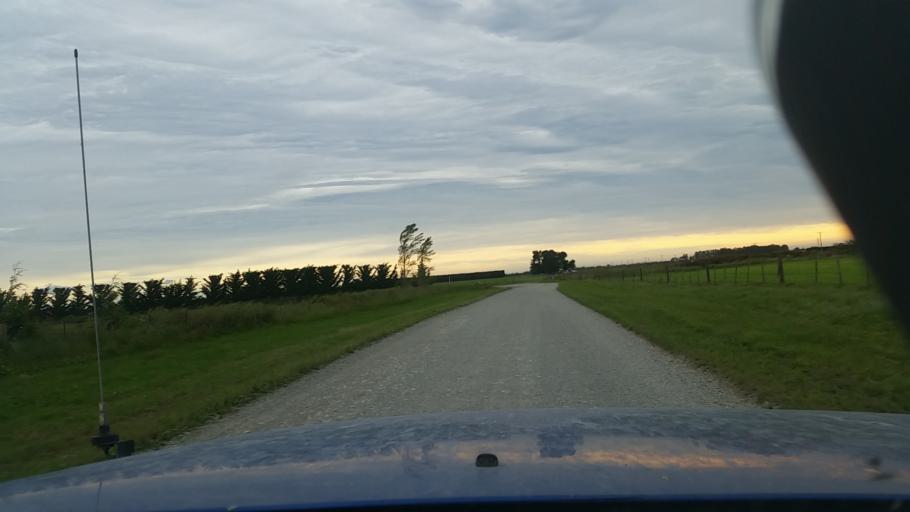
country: NZ
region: Canterbury
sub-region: Ashburton District
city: Tinwald
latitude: -44.0230
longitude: 171.5024
